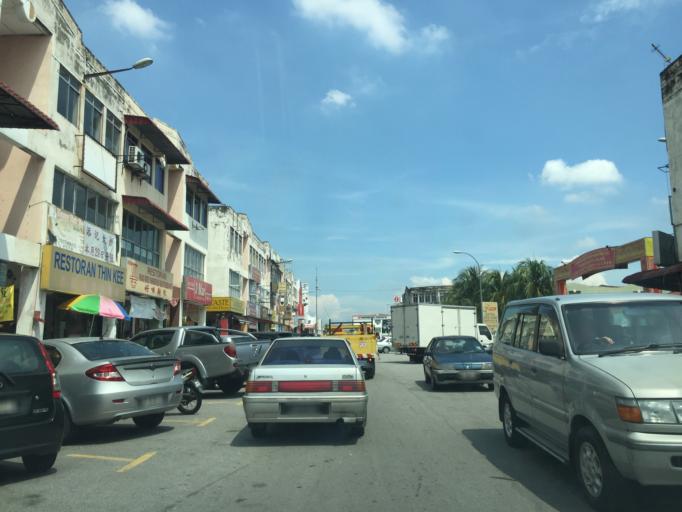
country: MY
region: Selangor
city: Klang
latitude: 3.0092
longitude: 101.4653
